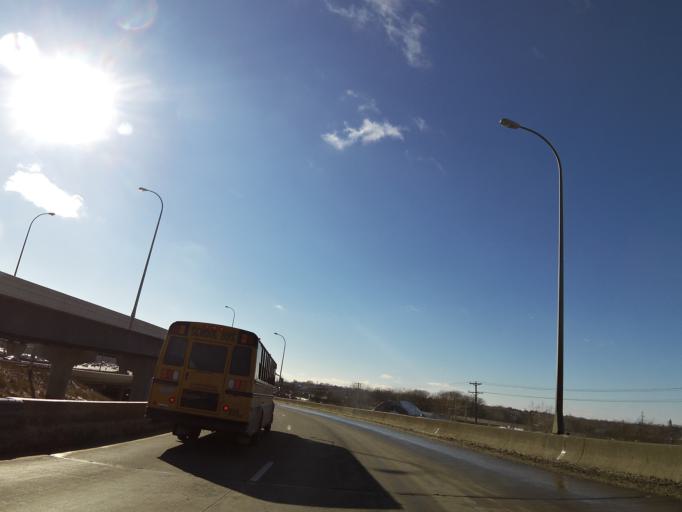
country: US
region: Minnesota
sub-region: Hennepin County
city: Minneapolis
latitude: 44.9754
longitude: -93.2906
